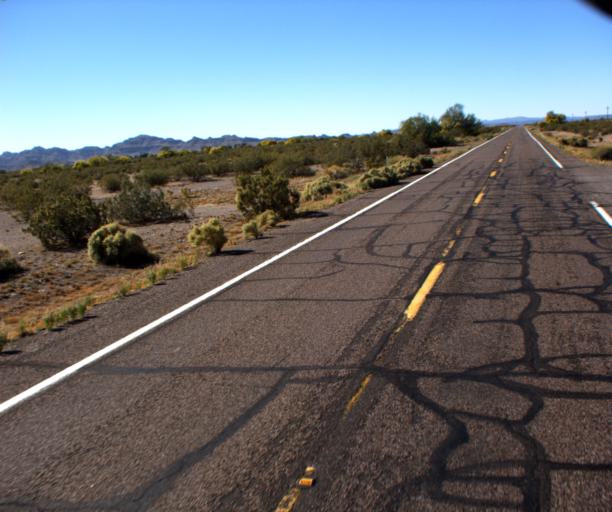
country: US
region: Arizona
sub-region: Maricopa County
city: Gila Bend
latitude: 32.7496
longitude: -112.8268
